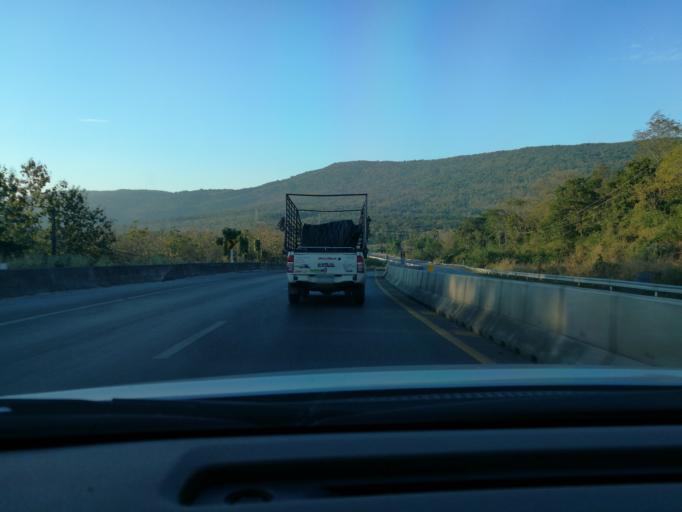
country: TH
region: Phitsanulok
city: Wang Thong
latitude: 16.8589
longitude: 100.5042
